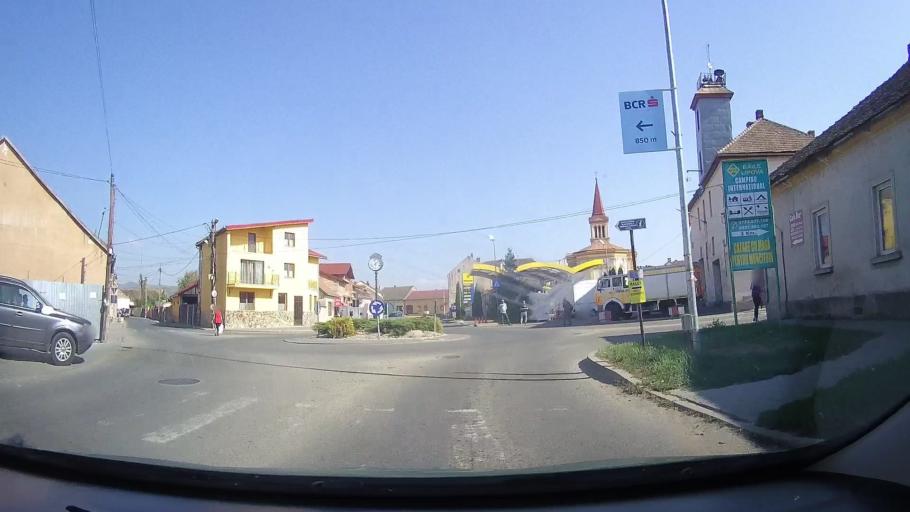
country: RO
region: Arad
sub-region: Oras Lipova
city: Lipova
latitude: 46.0891
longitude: 21.6908
